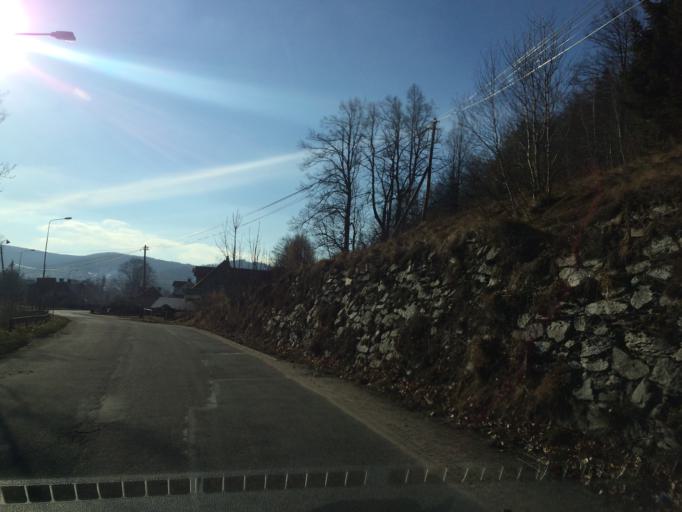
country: PL
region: Lower Silesian Voivodeship
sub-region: Powiat klodzki
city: Stronie Slaskie
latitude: 50.2973
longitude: 16.8922
